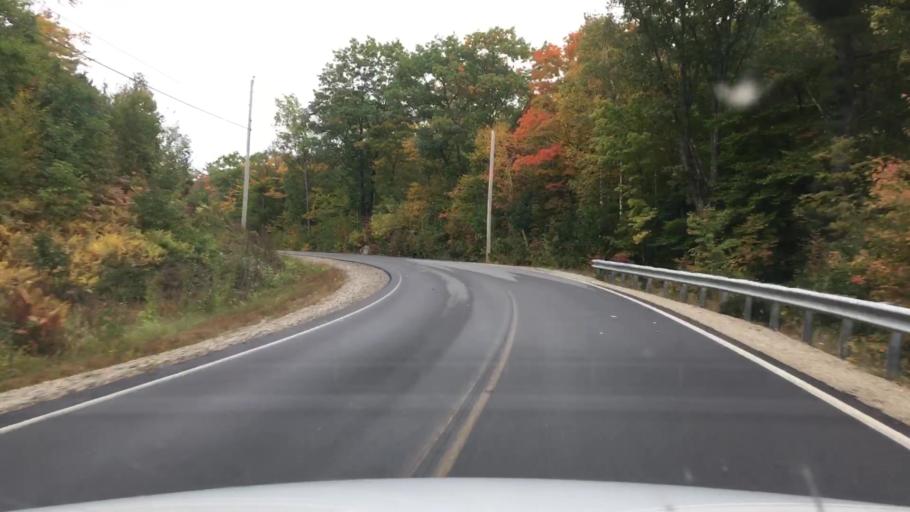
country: US
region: Maine
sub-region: Oxford County
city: Bethel
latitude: 44.2965
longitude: -70.7366
